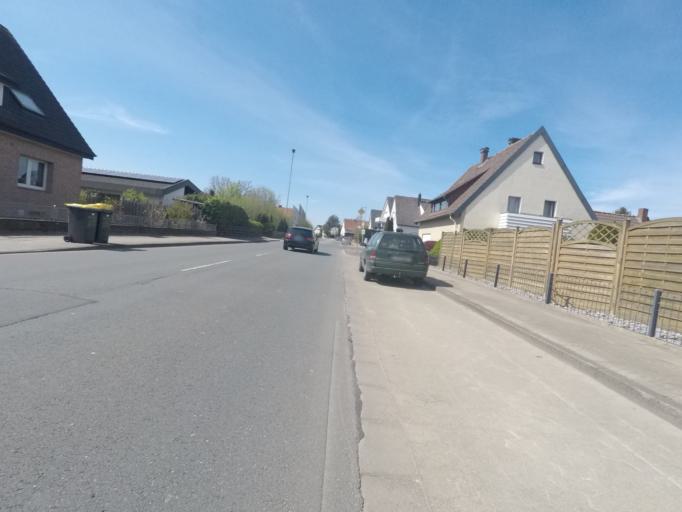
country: DE
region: North Rhine-Westphalia
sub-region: Regierungsbezirk Detmold
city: Herford
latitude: 52.0558
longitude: 8.6365
